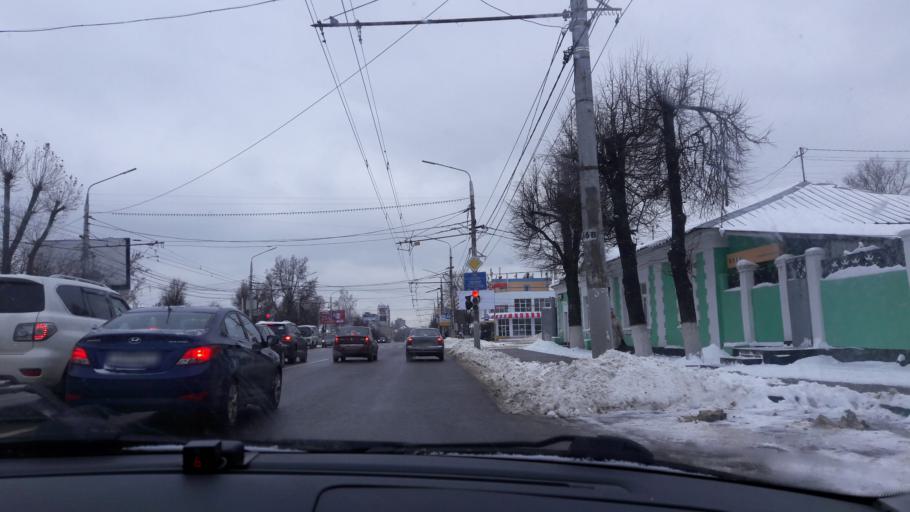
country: RU
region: Tula
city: Tula
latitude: 54.2261
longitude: 37.6285
